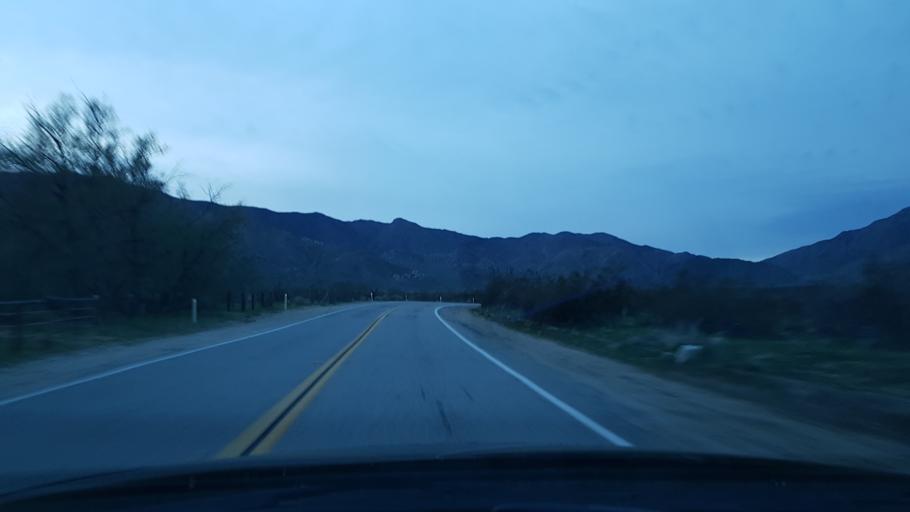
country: US
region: California
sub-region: San Diego County
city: Pine Valley
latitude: 32.9802
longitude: -116.4381
